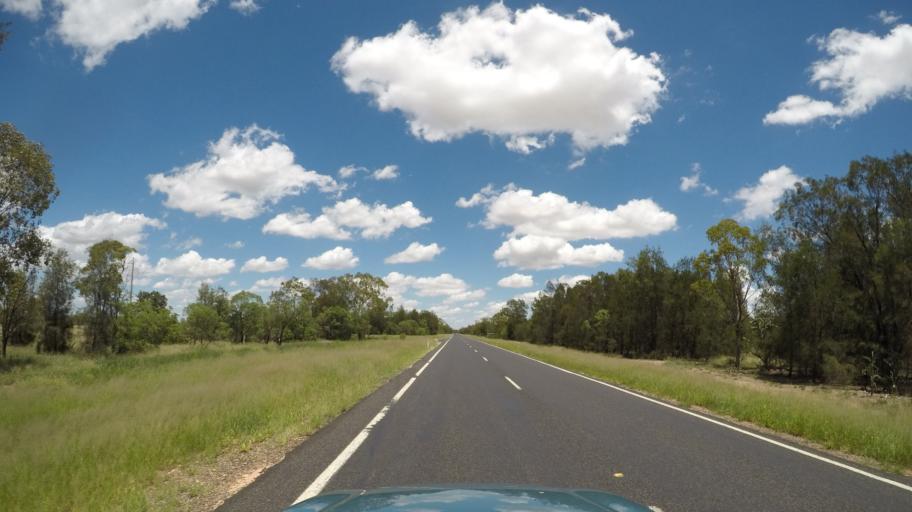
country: AU
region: Queensland
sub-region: Goondiwindi
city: Goondiwindi
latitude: -28.1700
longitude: 150.5848
